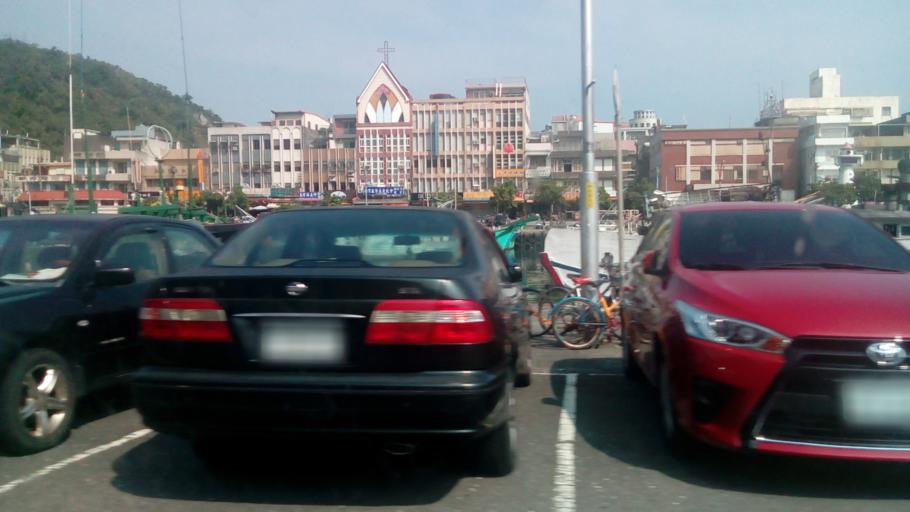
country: TW
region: Taiwan
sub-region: Yilan
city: Yilan
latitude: 24.5810
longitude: 121.8662
